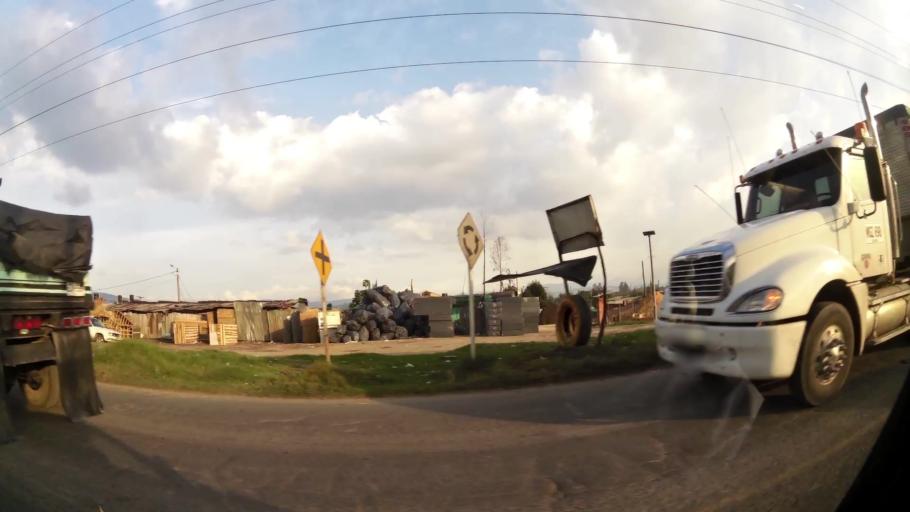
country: CO
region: Cundinamarca
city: Cota
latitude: 4.8015
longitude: -74.0974
